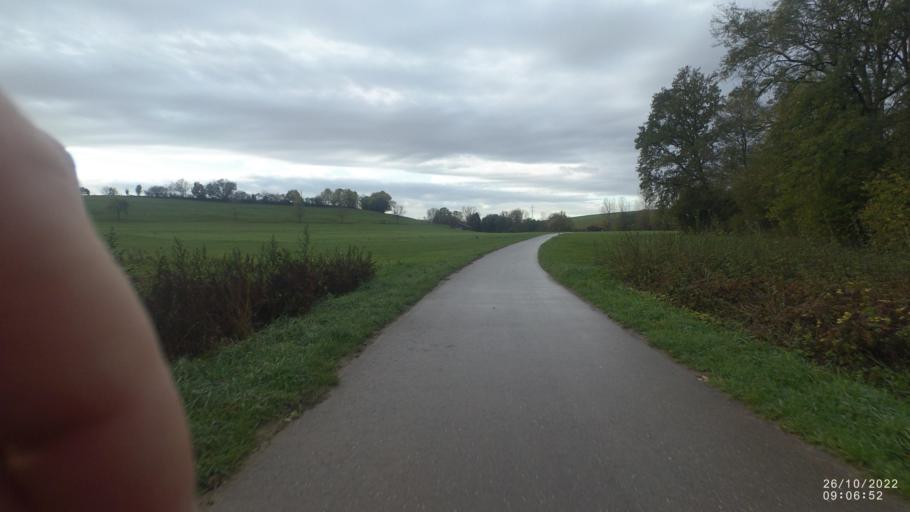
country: DE
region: Baden-Wuerttemberg
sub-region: Regierungsbezirk Stuttgart
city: Heiningen
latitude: 48.6782
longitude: 9.6691
